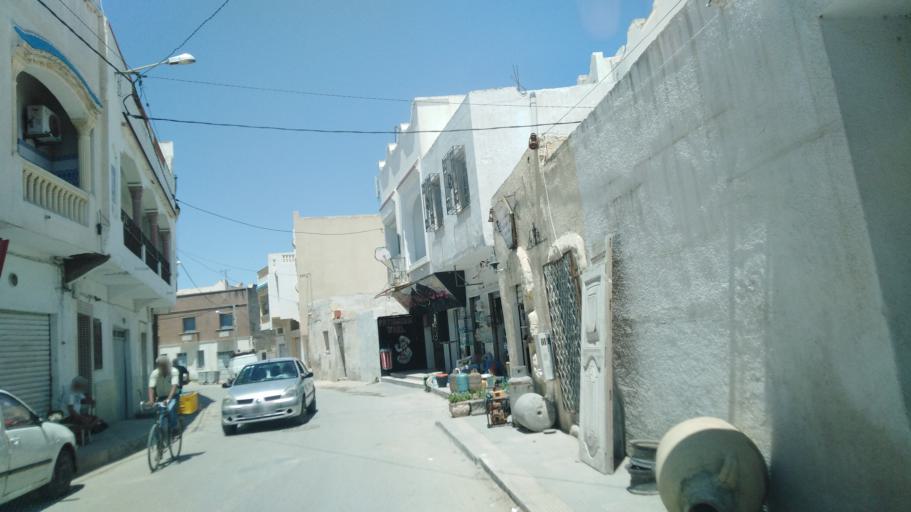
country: TN
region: Al Mahdiyah
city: Ksour Essaf
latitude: 35.4174
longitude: 10.9916
